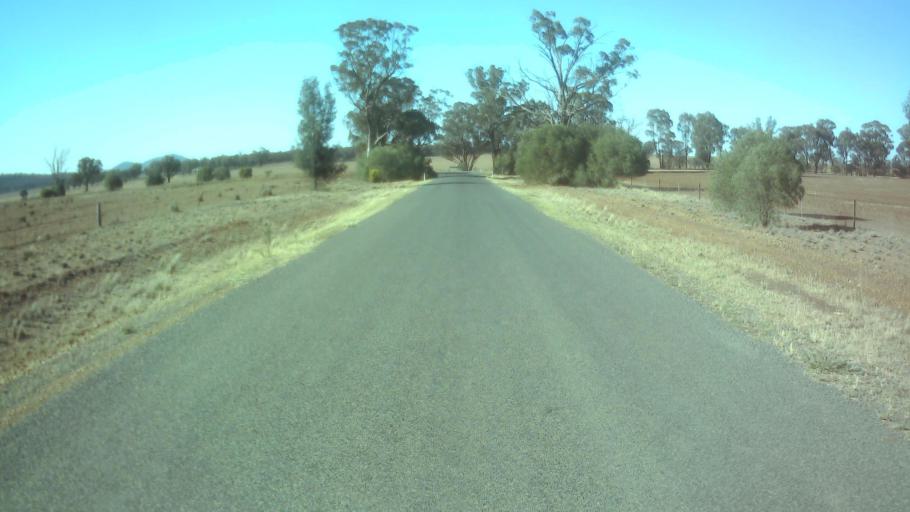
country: AU
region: New South Wales
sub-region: Forbes
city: Forbes
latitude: -33.6958
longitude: 147.8076
